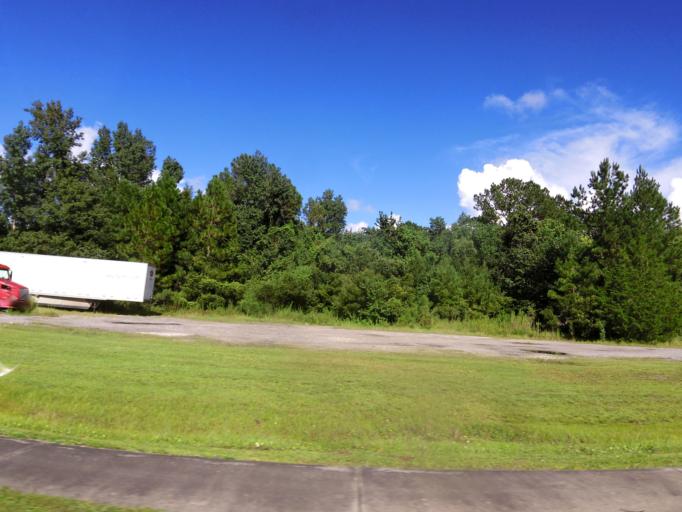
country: US
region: Georgia
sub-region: Camden County
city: Woodbine
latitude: 30.9530
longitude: -81.7205
